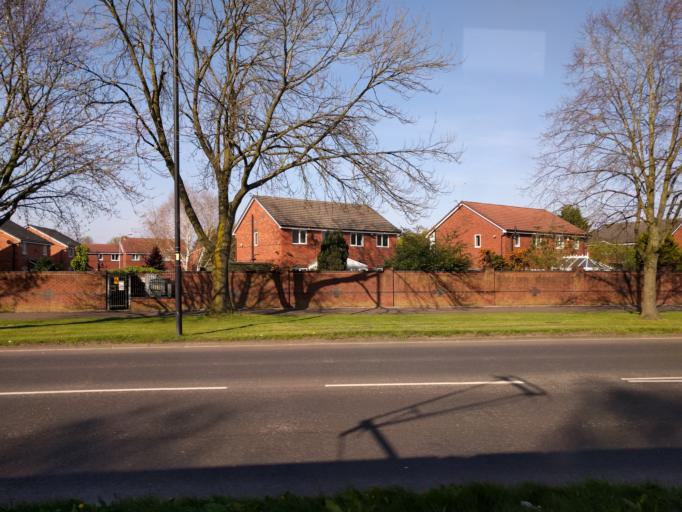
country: GB
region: England
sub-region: Manchester
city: Ringway
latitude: 53.3755
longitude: -2.2539
